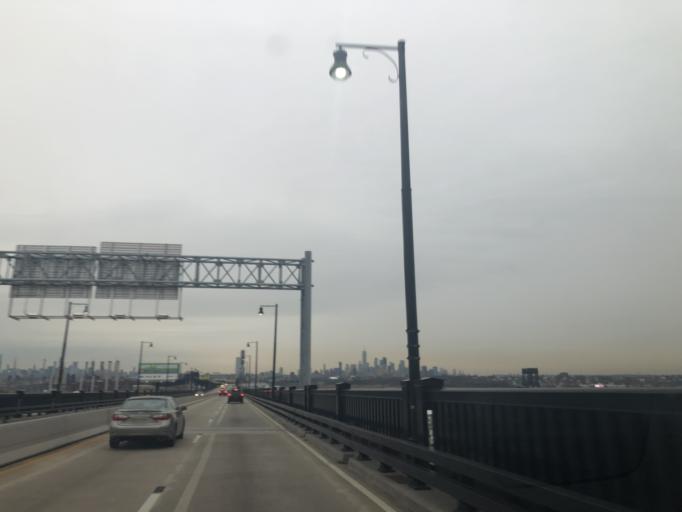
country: US
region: New Jersey
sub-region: Hudson County
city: Jersey City
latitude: 40.7347
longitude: -74.1153
